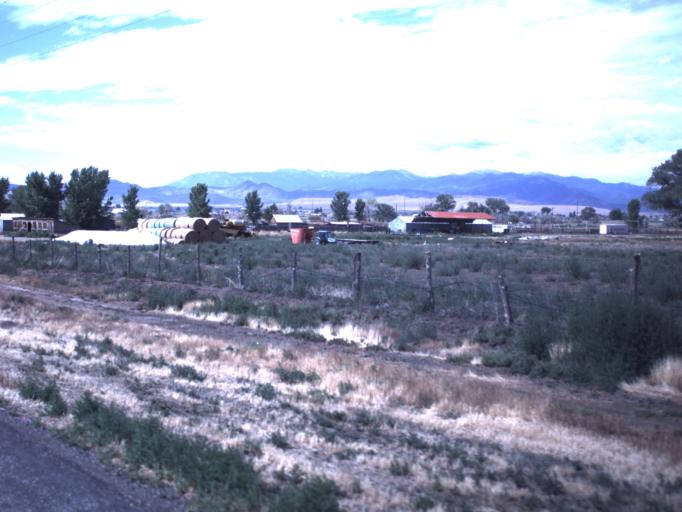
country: US
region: Utah
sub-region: Sevier County
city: Monroe
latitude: 38.6798
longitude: -112.1216
